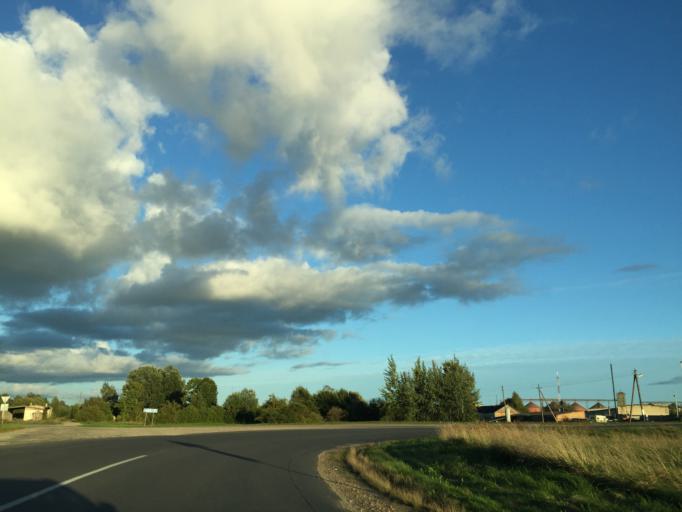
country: LV
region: Saldus Rajons
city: Saldus
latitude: 56.6889
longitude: 22.4580
